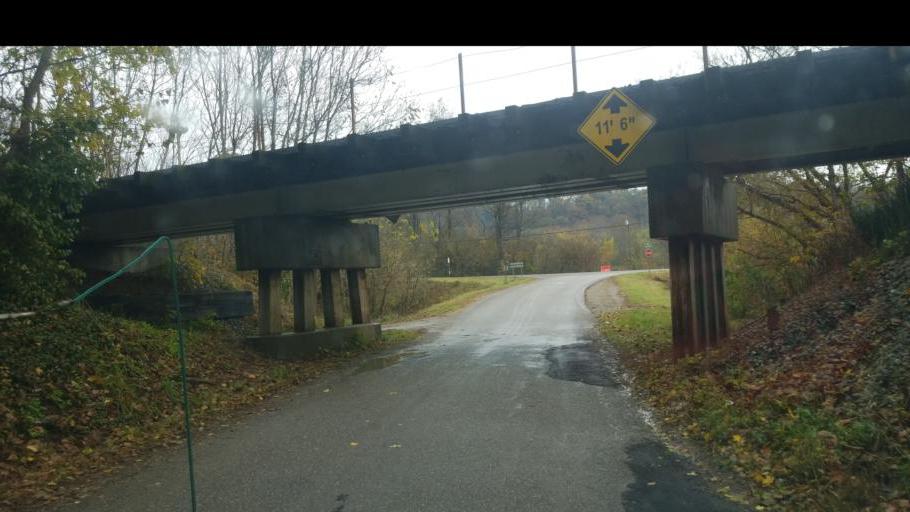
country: US
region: Ohio
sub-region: Washington County
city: Beverly
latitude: 39.5508
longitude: -81.6498
